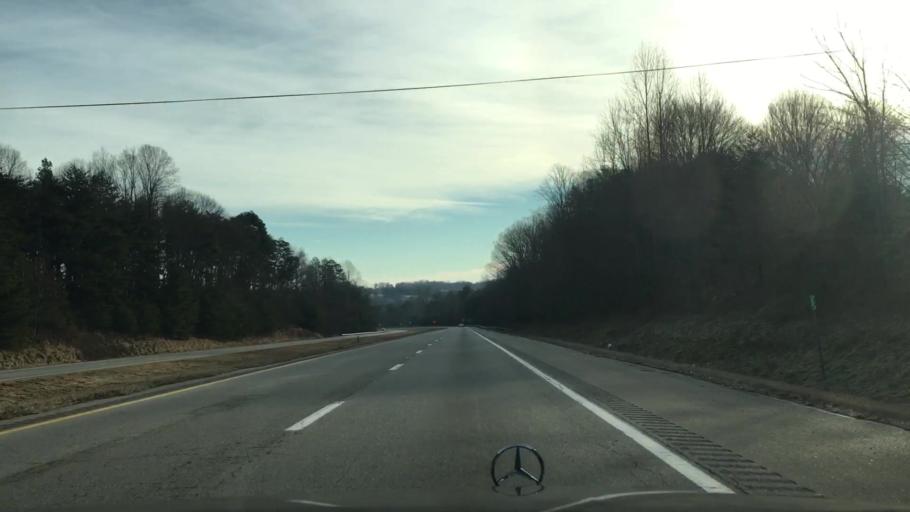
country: US
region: Virginia
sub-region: City of Danville
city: Danville
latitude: 36.5455
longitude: -79.4221
